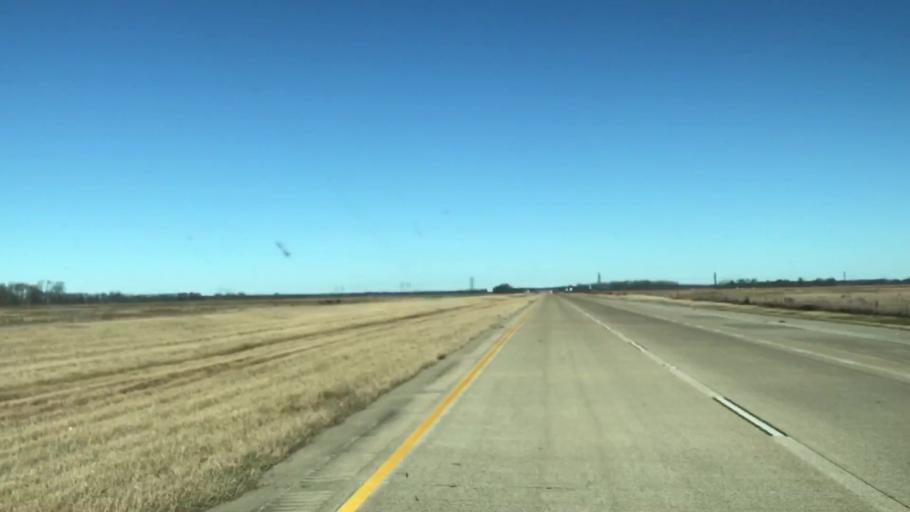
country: US
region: Louisiana
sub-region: Caddo Parish
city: Oil City
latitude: 32.7080
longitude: -93.8637
